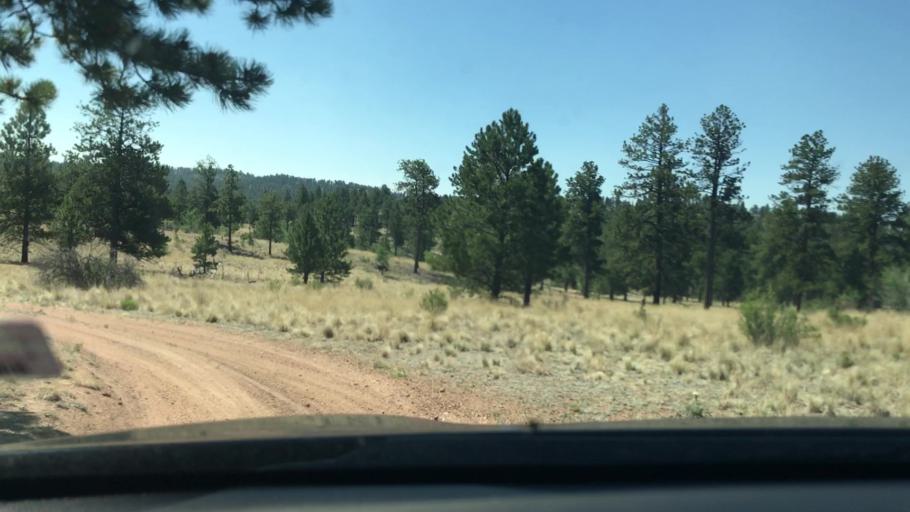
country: US
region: Colorado
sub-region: Teller County
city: Woodland Park
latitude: 39.0004
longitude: -105.3461
